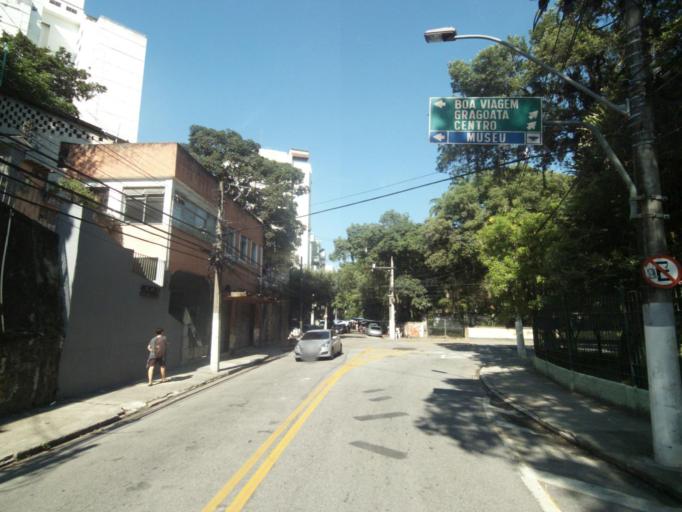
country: BR
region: Rio de Janeiro
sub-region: Niteroi
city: Niteroi
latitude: -22.9044
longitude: -43.1297
